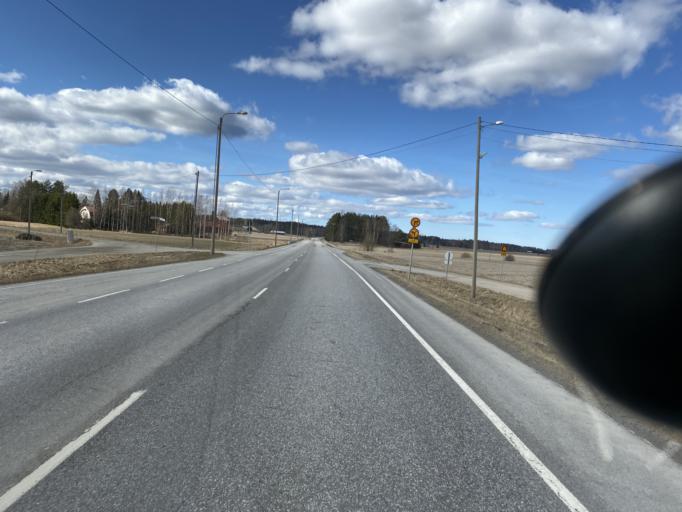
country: FI
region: Satakunta
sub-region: Pori
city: Huittinen
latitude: 61.1774
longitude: 22.6002
